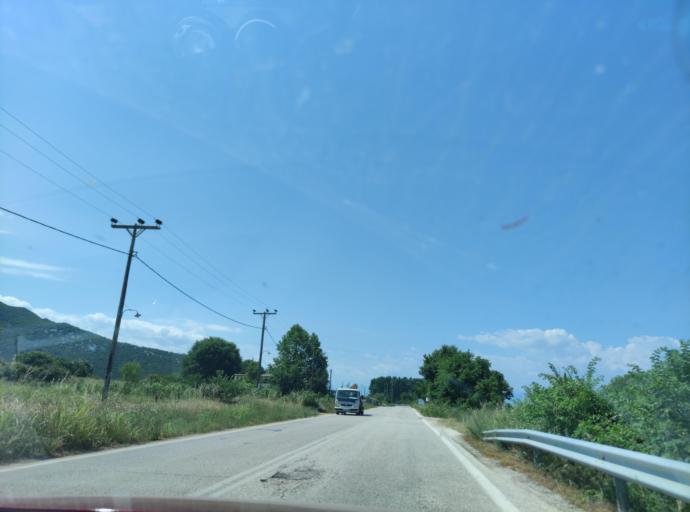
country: GR
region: East Macedonia and Thrace
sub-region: Nomos Kavalas
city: Palaiochori
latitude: 40.9595
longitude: 24.1887
